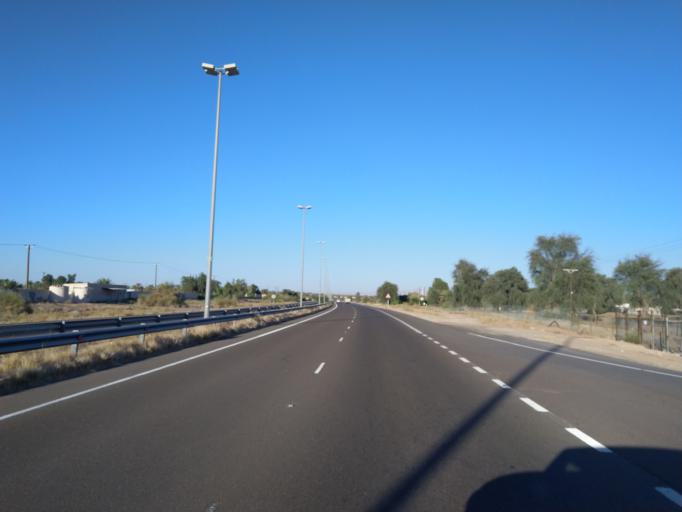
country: OM
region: Al Buraimi
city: Al Buraymi
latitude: 24.5545
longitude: 55.6889
